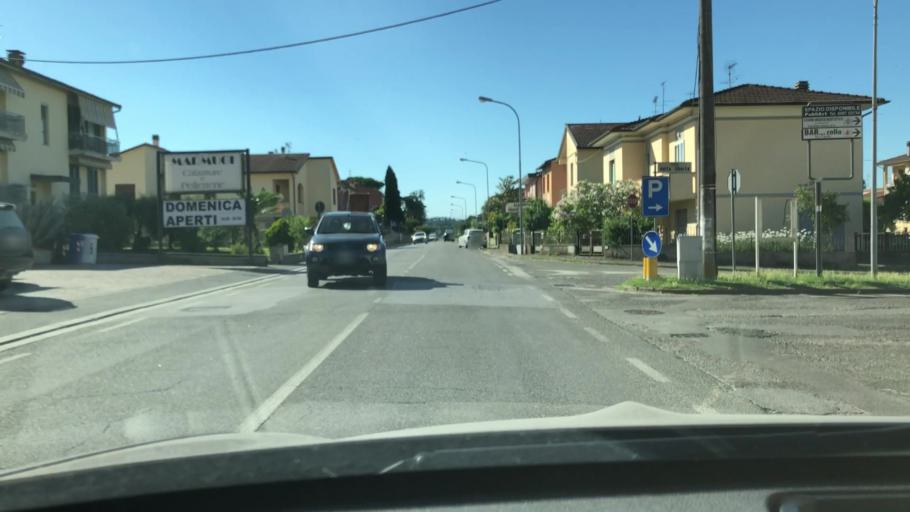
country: IT
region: Tuscany
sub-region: Province of Pisa
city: Forcoli
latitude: 43.6019
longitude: 10.7085
